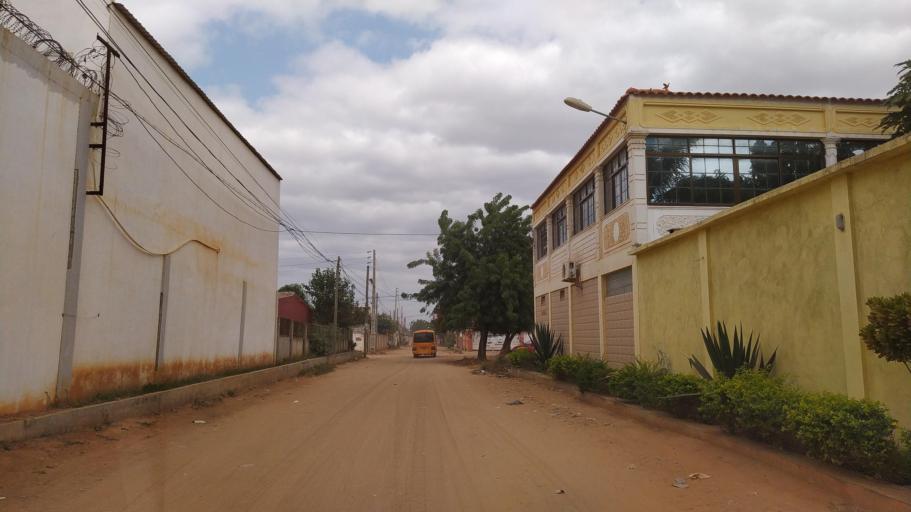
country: AO
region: Luanda
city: Luanda
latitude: -8.9260
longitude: 13.2614
